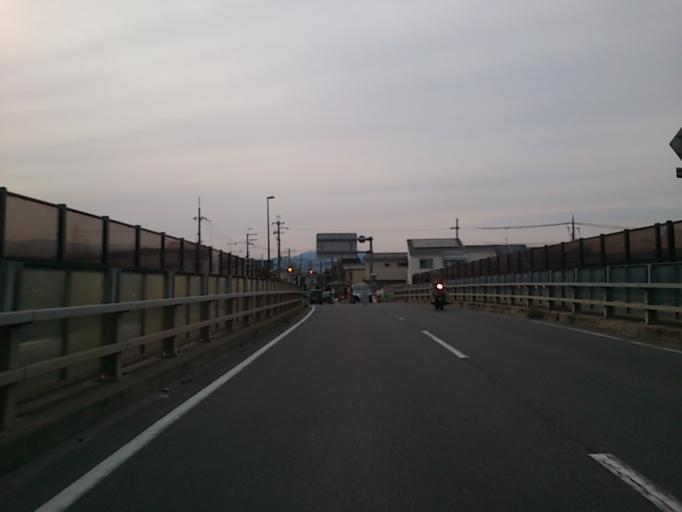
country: JP
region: Kyoto
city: Yawata
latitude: 34.8969
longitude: 135.7183
